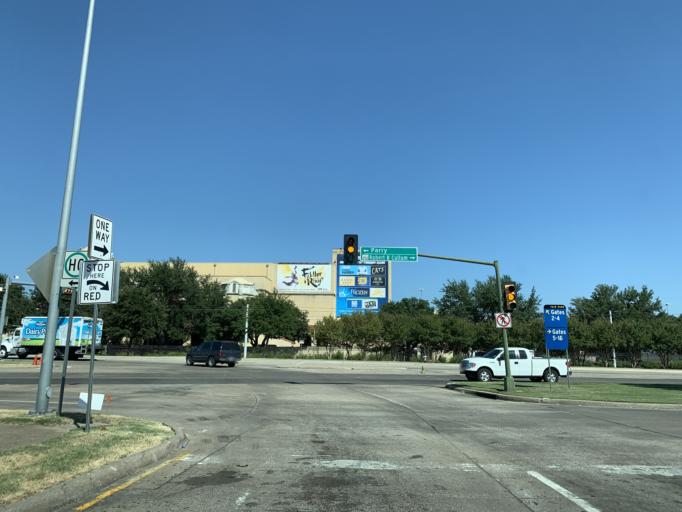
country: US
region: Texas
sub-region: Dallas County
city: Dallas
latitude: 32.7805
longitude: -96.7673
